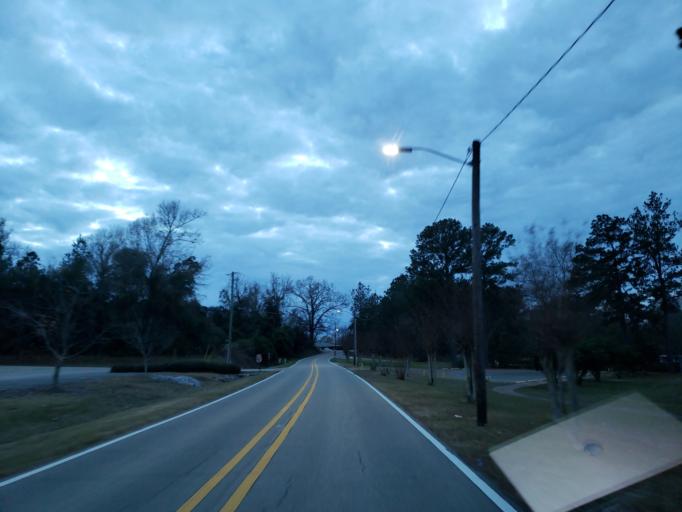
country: US
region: Mississippi
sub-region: Forrest County
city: Petal
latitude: 31.3406
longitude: -89.2523
